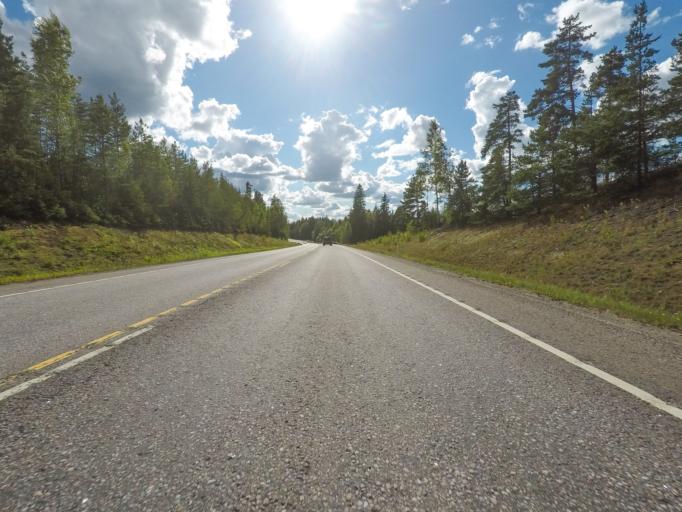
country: FI
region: Uusimaa
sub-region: Helsinki
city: Nurmijaervi
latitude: 60.5432
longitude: 24.7275
